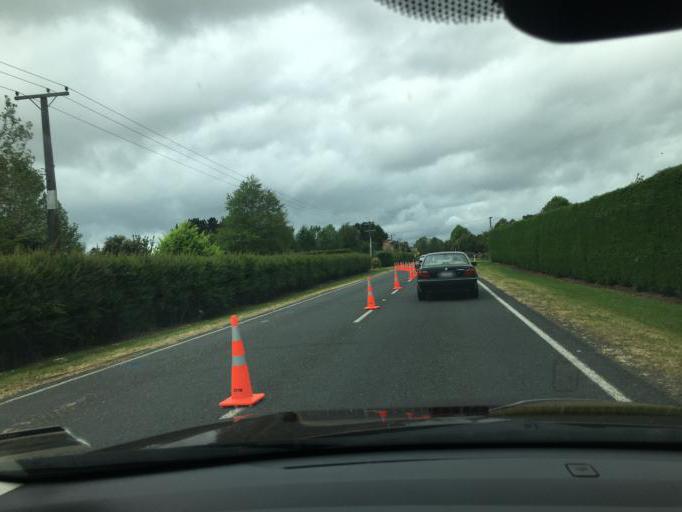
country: NZ
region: Waikato
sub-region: Waipa District
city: Cambridge
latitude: -37.9165
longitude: 175.4442
